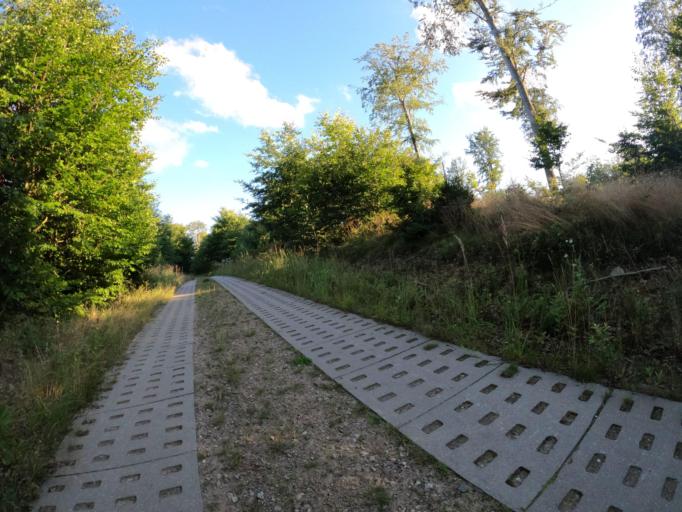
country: PL
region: West Pomeranian Voivodeship
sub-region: Powiat drawski
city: Drawsko Pomorskie
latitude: 53.6505
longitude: 15.9055
